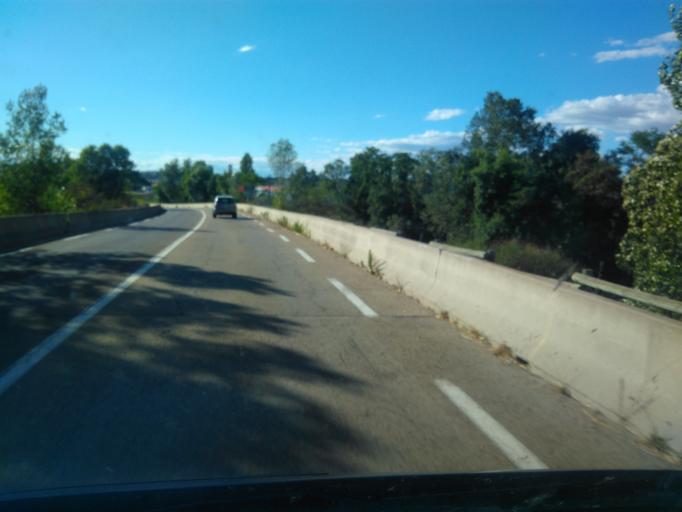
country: FR
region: Languedoc-Roussillon
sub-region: Departement du Gard
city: Saint-Gilles
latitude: 43.6663
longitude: 4.4523
